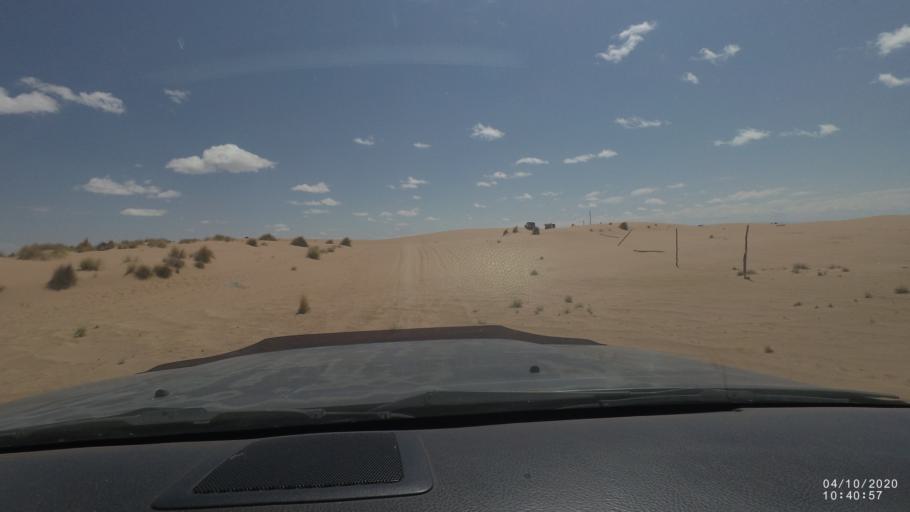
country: BO
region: Oruro
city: Poopo
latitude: -18.7049
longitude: -67.4719
